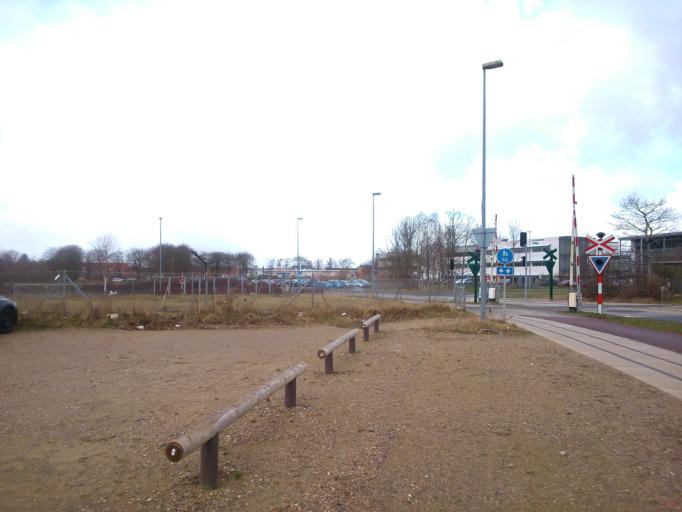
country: DK
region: Central Jutland
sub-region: Holstebro Kommune
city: Holstebro
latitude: 56.3700
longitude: 8.6218
